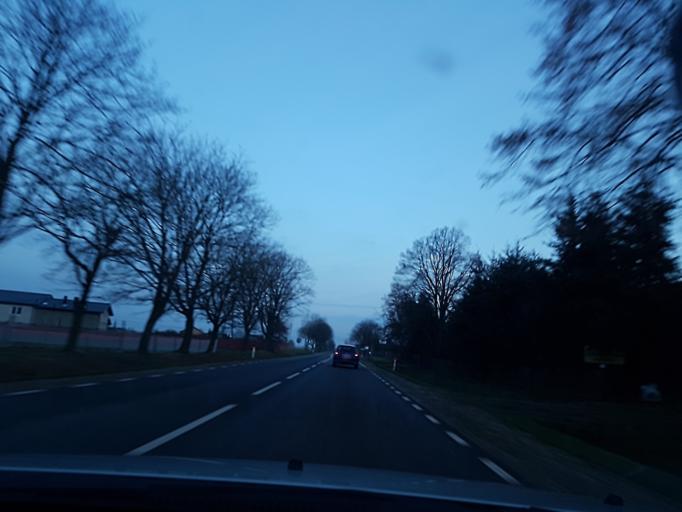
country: PL
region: Masovian Voivodeship
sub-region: Powiat plocki
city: Wyszogrod
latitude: 52.4046
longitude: 20.1462
